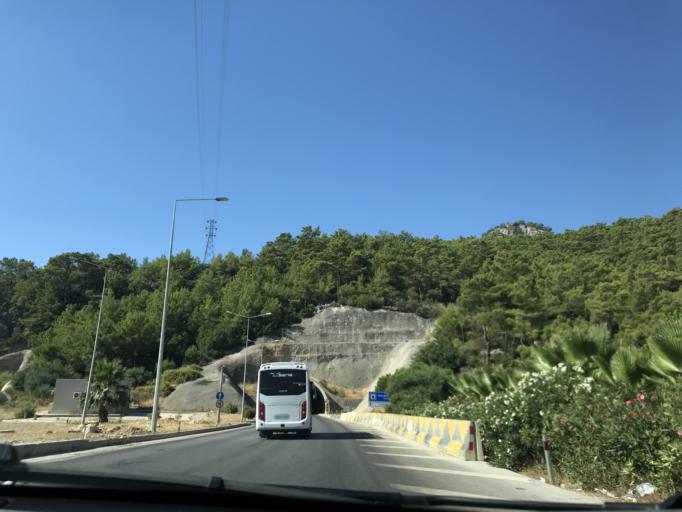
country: TR
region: Antalya
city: Cakirlar
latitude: 36.7665
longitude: 30.5706
